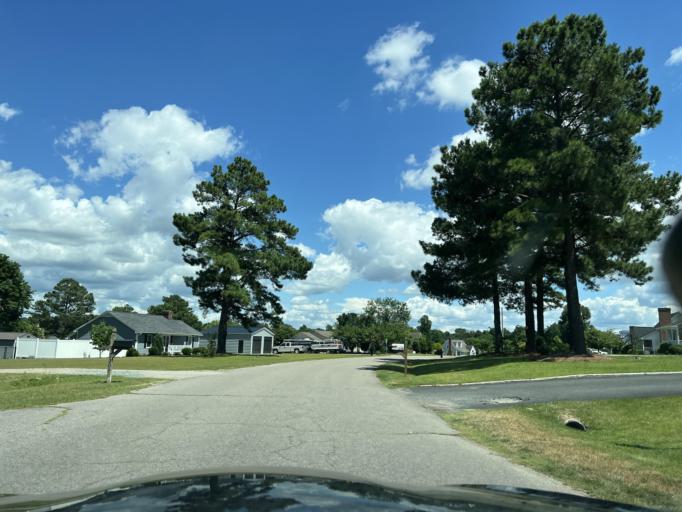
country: US
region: North Carolina
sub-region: Lee County
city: Sanford
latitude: 35.4339
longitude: -79.1623
